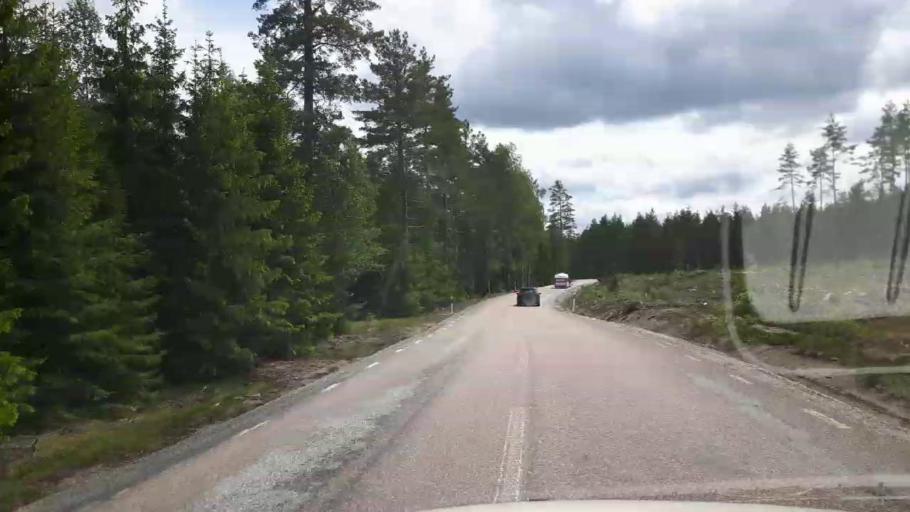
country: SE
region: Vaestmanland
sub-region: Skinnskattebergs Kommun
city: Skinnskatteberg
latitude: 59.8206
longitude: 15.8369
